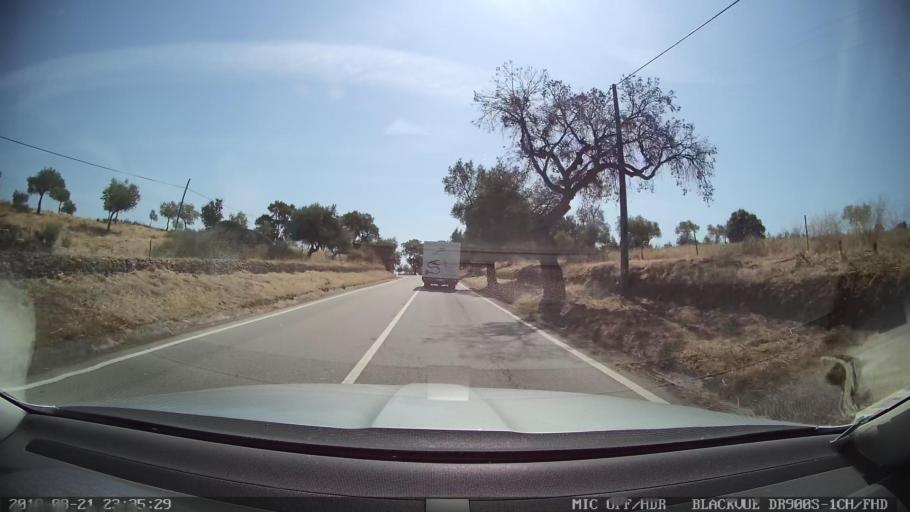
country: PT
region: Guarda
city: Alcains
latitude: 39.8781
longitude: -7.3875
